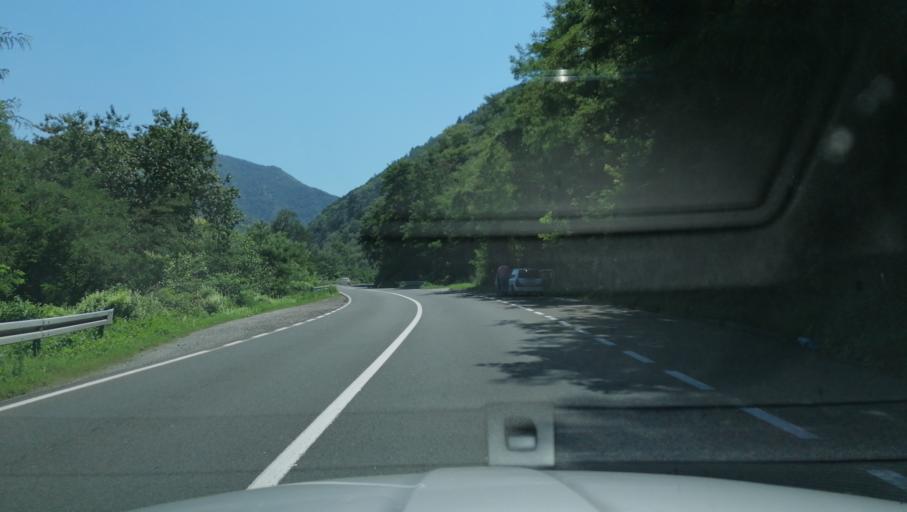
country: RS
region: Central Serbia
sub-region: Raski Okrug
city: Kraljevo
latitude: 43.6270
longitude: 20.5450
